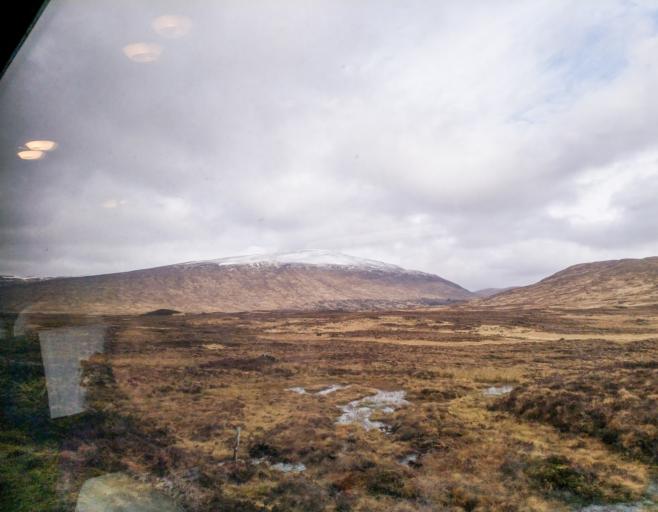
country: GB
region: Scotland
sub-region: Highland
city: Spean Bridge
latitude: 56.7477
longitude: -4.6732
